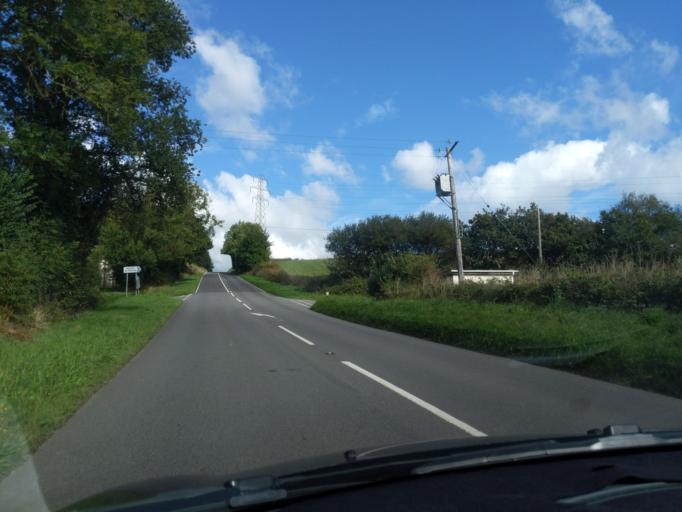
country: GB
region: England
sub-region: Devon
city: Holsworthy
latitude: 50.8915
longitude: -4.2745
